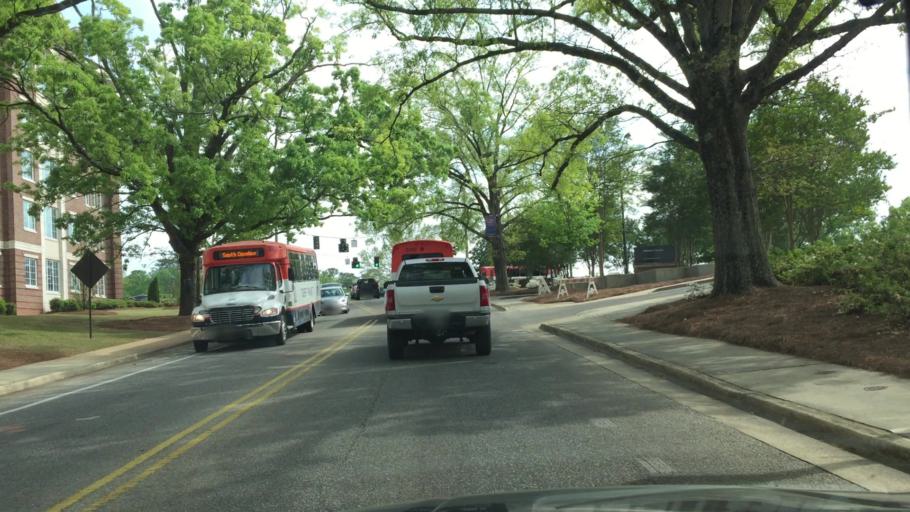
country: US
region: Alabama
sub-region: Lee County
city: Auburn
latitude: 32.5985
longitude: -85.4905
